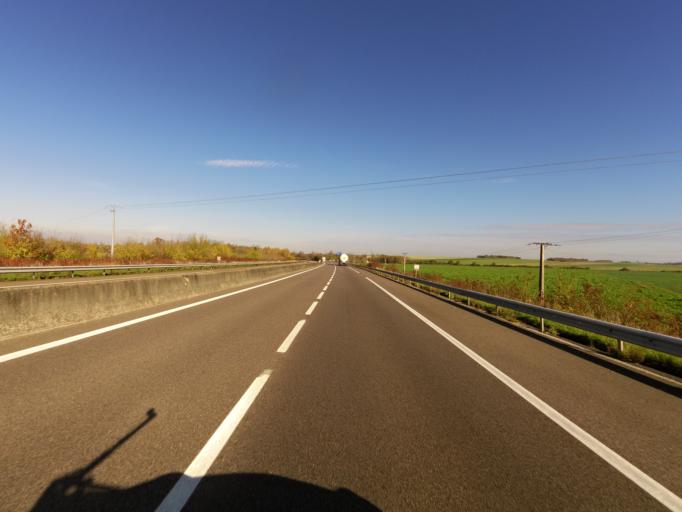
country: FR
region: Champagne-Ardenne
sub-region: Departement de la Marne
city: Fagnieres
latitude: 49.0017
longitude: 4.2983
